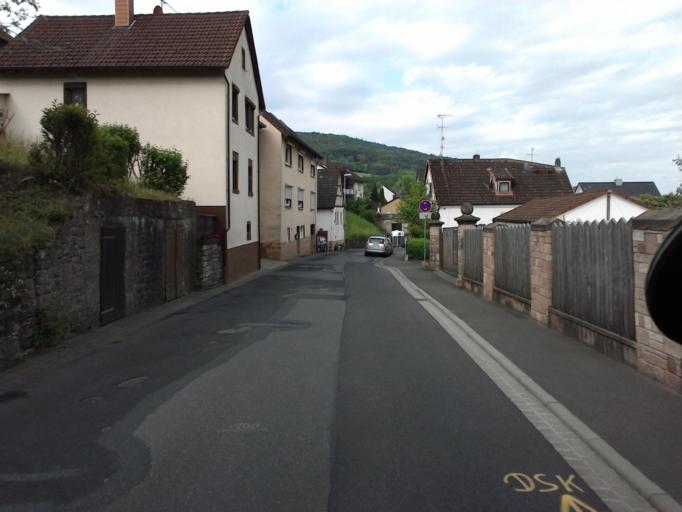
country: DE
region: Bavaria
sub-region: Regierungsbezirk Unterfranken
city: Waldaschaff
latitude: 49.9733
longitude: 9.3078
